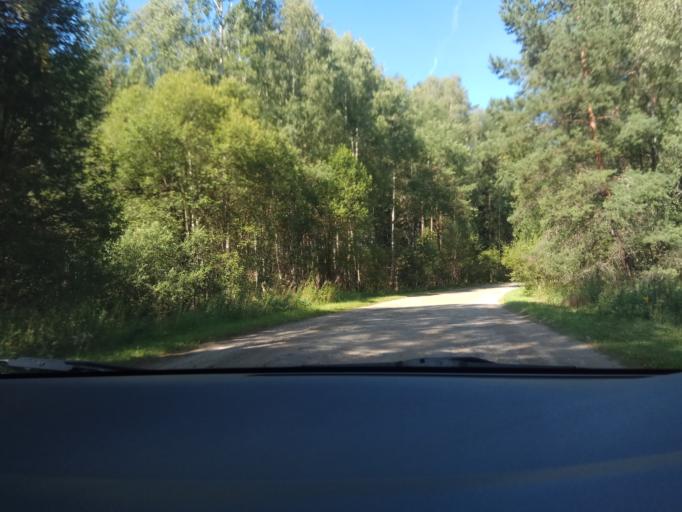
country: RU
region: Vladimir
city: Dobryatino
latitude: 55.7389
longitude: 41.4290
